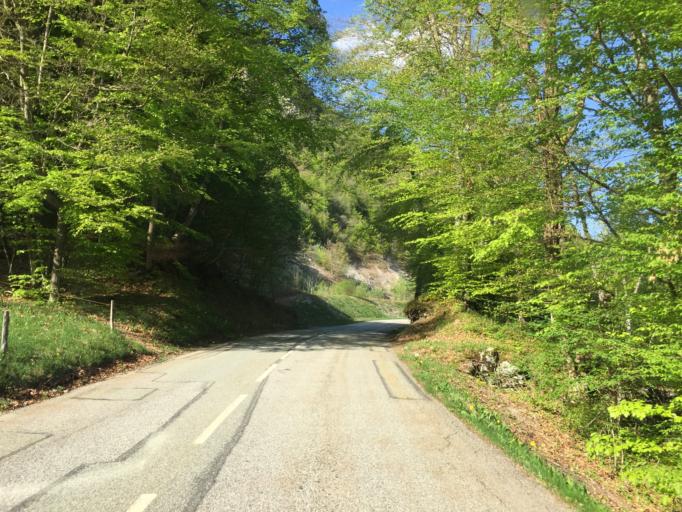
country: FR
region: Rhone-Alpes
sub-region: Departement de la Savoie
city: Frontenex
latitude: 45.6667
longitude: 6.2986
